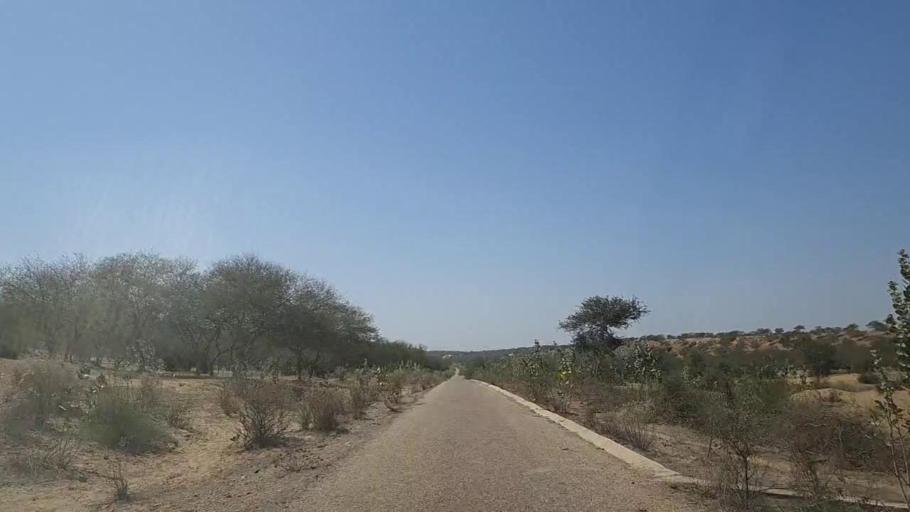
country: PK
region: Sindh
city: Mithi
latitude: 24.8177
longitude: 69.6622
